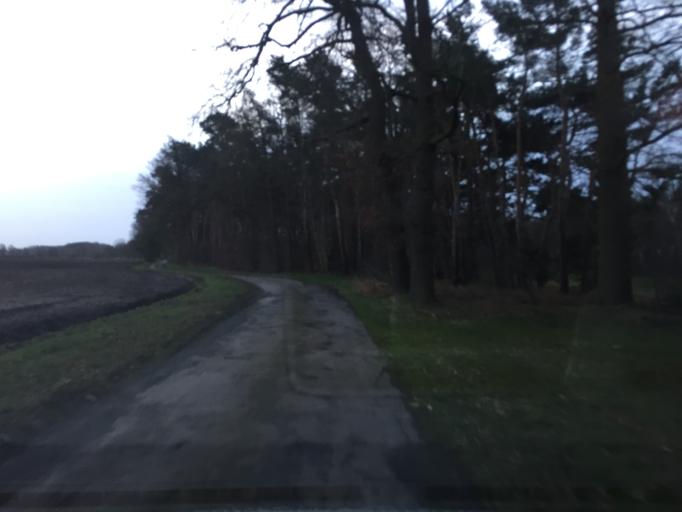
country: DE
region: Lower Saxony
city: Kirchdorf
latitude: 52.6121
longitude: 8.8657
